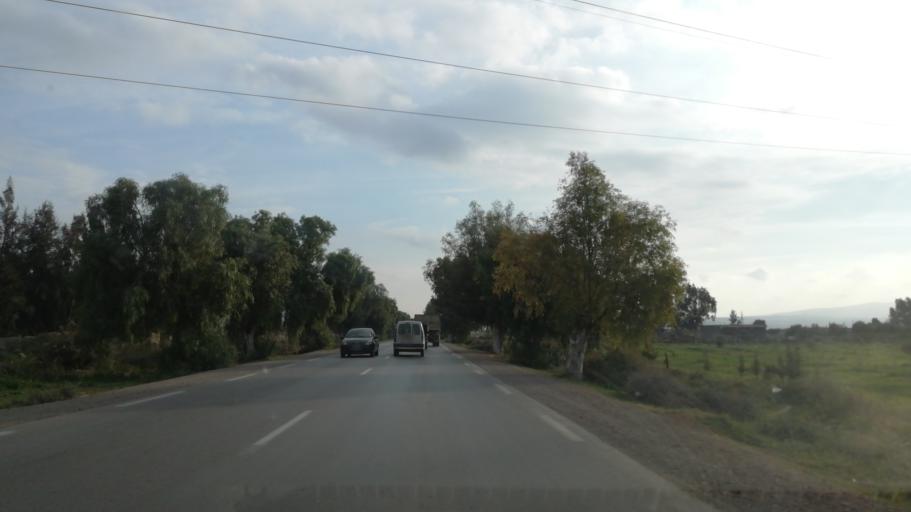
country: DZ
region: Mascara
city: Mascara
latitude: 35.6372
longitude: 0.0607
